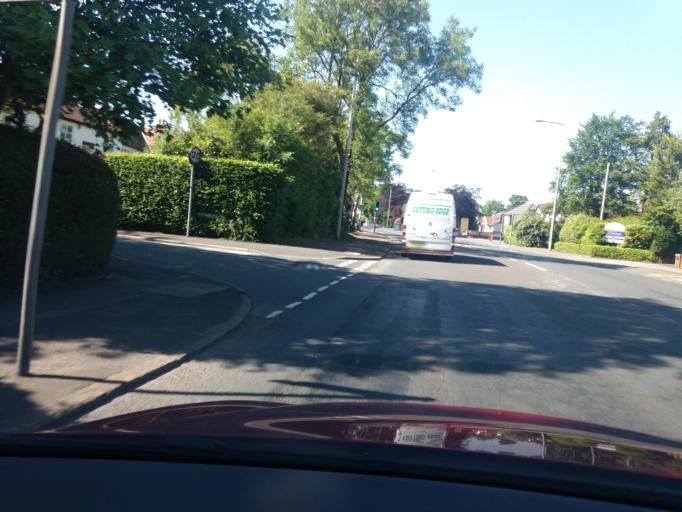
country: GB
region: England
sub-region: Lancashire
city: Preston
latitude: 53.7960
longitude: -2.7143
